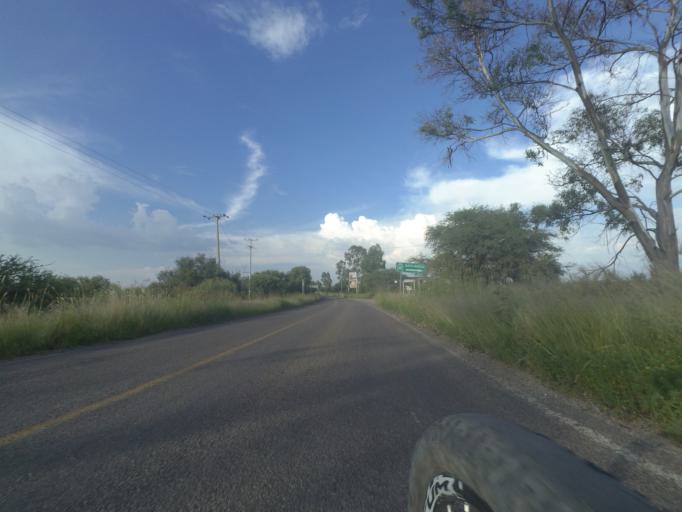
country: MX
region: Aguascalientes
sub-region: Aguascalientes
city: Penuelas (El Cienegal)
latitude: 21.7192
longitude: -102.3662
